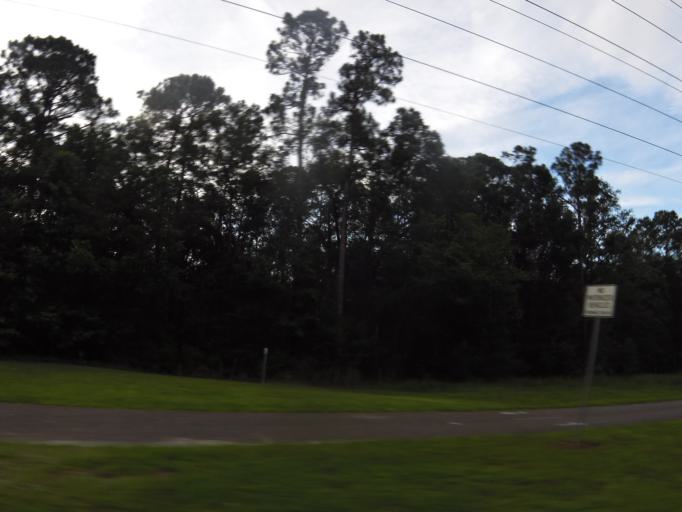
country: US
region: Florida
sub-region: Duval County
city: Jacksonville
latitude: 30.3444
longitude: -81.7814
